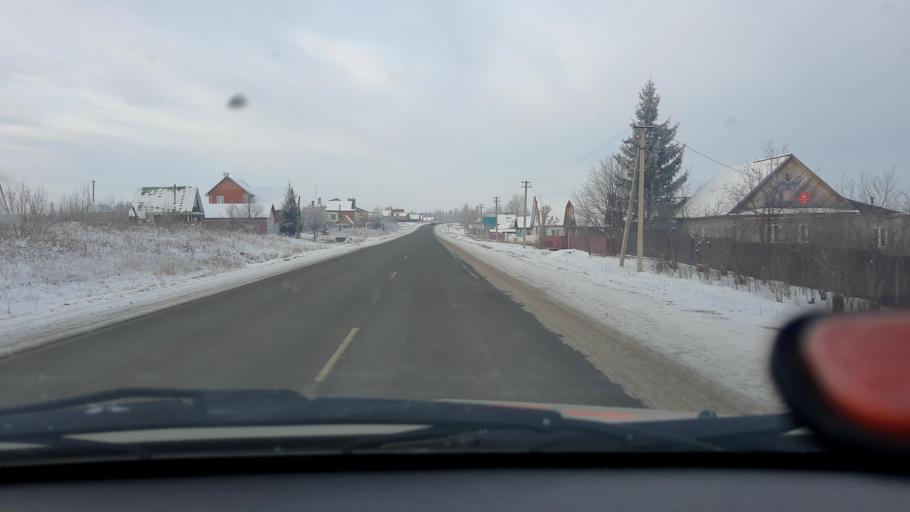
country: RU
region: Bashkortostan
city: Avdon
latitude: 54.3704
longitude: 55.8187
